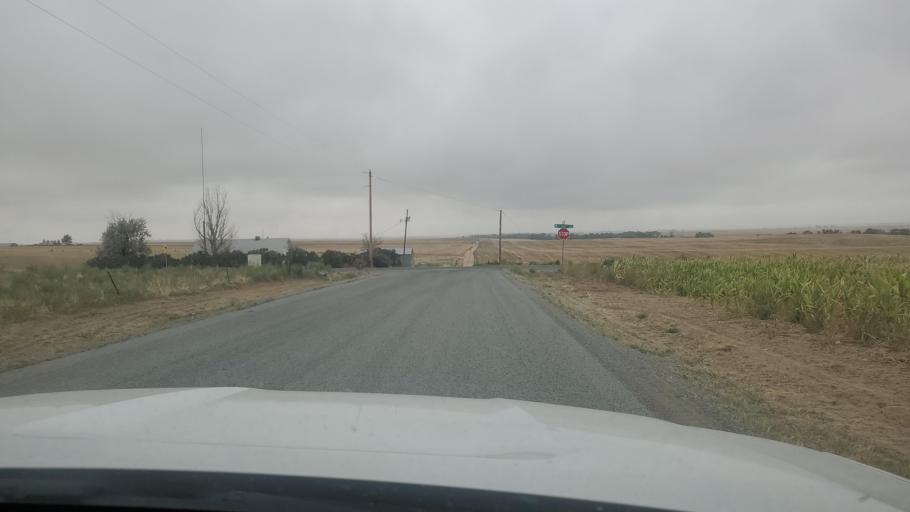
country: US
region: Colorado
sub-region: Weld County
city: Lochbuie
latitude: 39.9142
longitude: -104.6027
